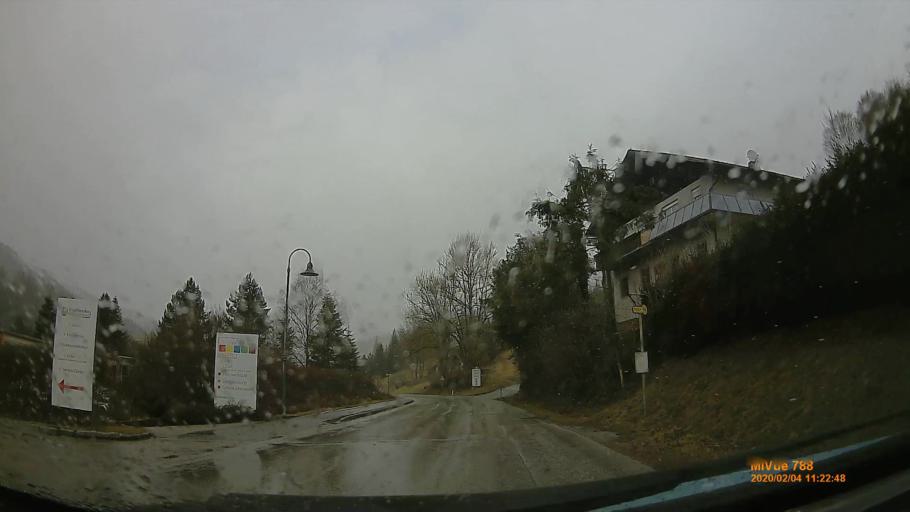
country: AT
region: Styria
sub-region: Politischer Bezirk Bruck-Muerzzuschlag
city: Muerzzuschlag
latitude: 47.6142
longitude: 15.6678
